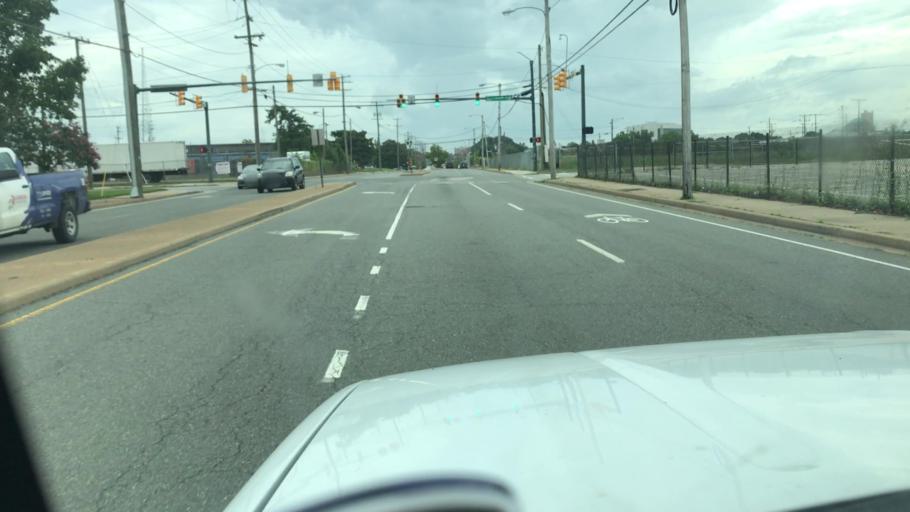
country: US
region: Virginia
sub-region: City of Richmond
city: Richmond
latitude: 37.5707
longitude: -77.4608
